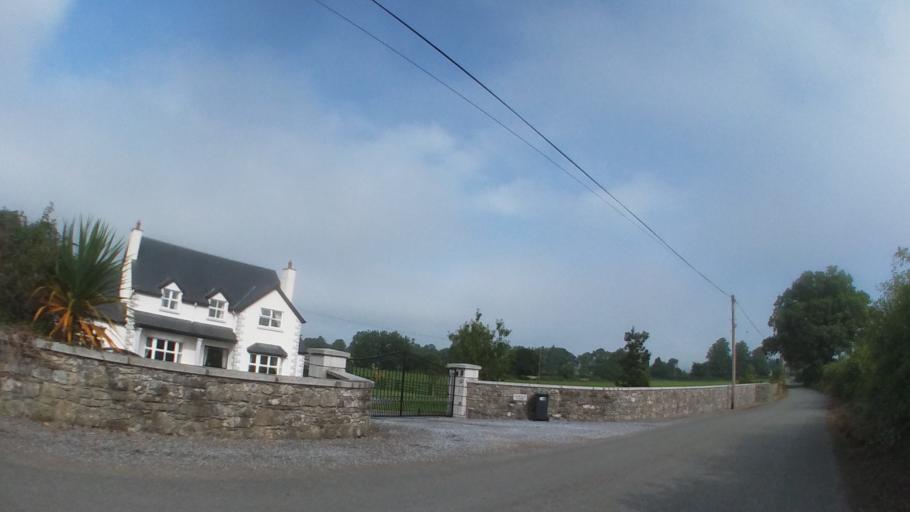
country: IE
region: Leinster
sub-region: Kilkenny
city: Kilkenny
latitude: 52.6849
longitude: -7.1870
